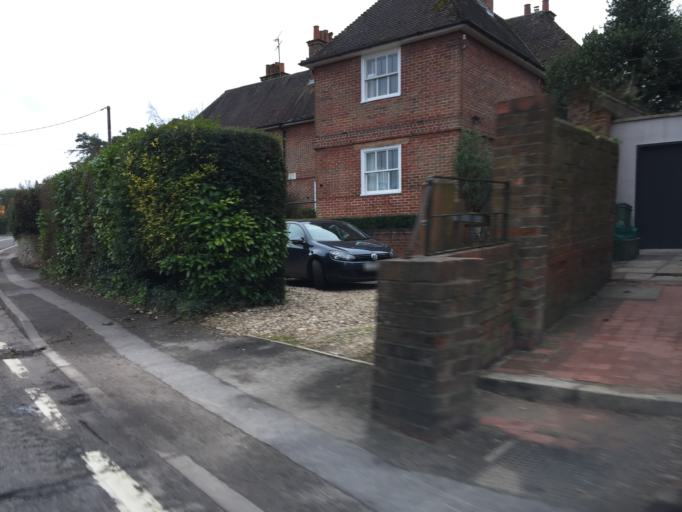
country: GB
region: England
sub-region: West Berkshire
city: Basildon
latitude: 51.5052
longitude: -1.1237
